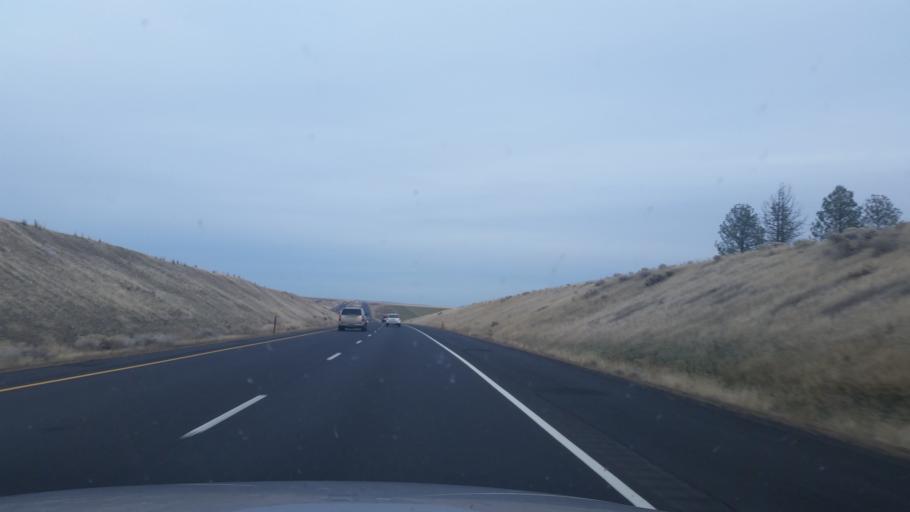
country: US
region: Washington
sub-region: Grant County
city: Warden
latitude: 47.0858
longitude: -118.8444
